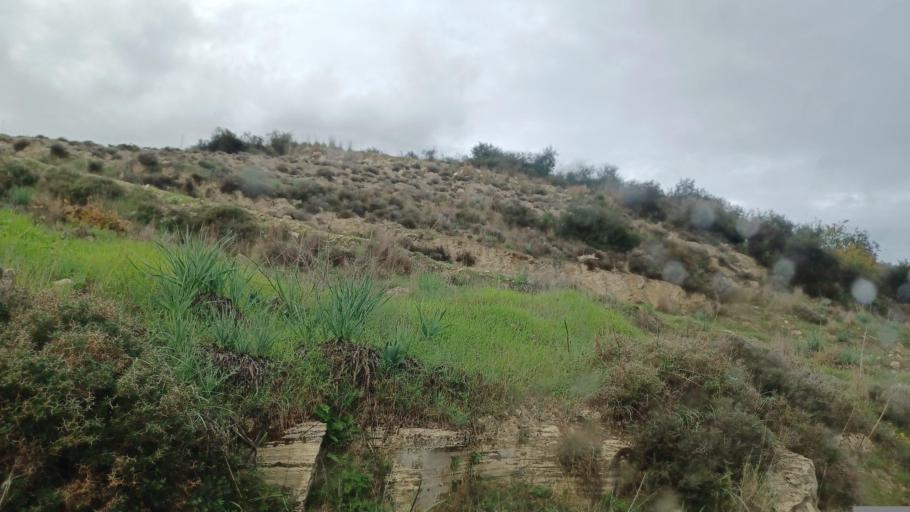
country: CY
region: Pafos
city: Mesogi
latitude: 34.8700
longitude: 32.5324
